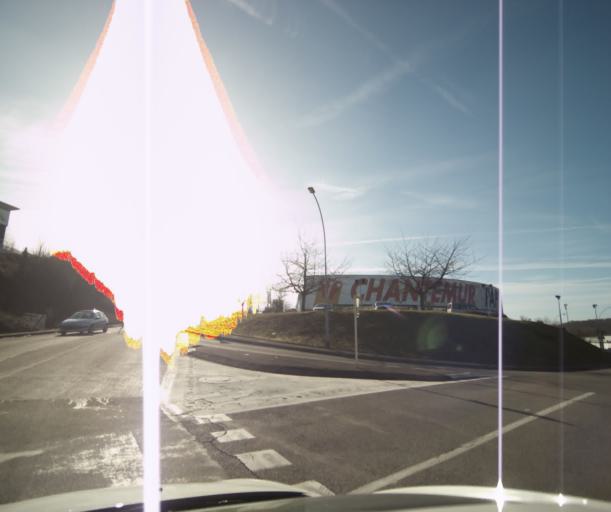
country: FR
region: Franche-Comte
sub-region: Departement du Doubs
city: Avanne-Aveney
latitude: 47.2147
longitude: 5.9511
